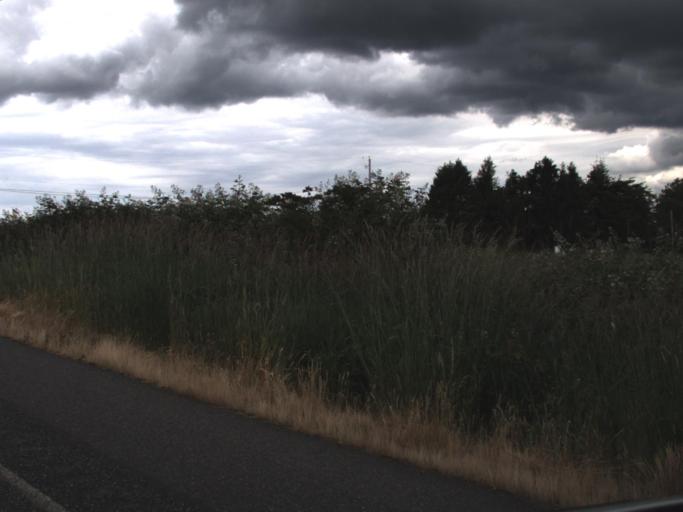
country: US
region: Washington
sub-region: Whatcom County
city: Ferndale
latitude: 48.8917
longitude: -122.6488
